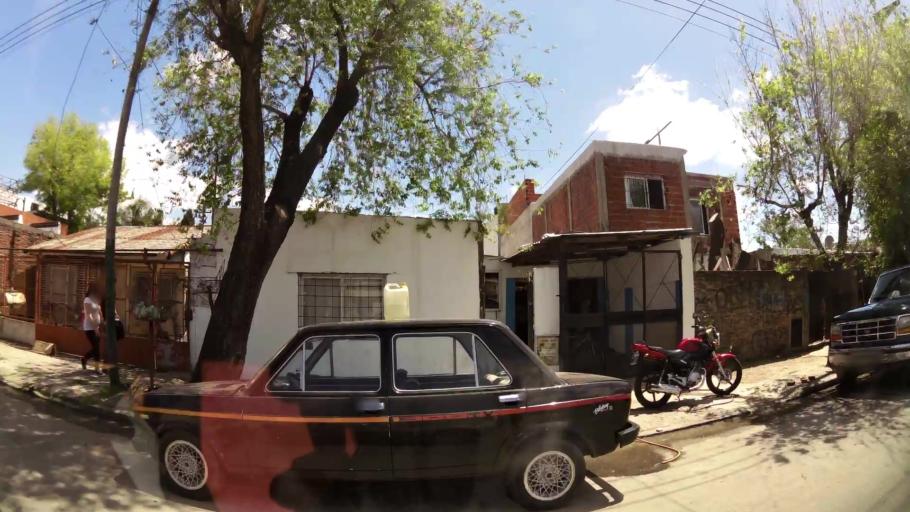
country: AR
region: Buenos Aires
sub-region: Partido de Lomas de Zamora
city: Lomas de Zamora
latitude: -34.7366
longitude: -58.4178
